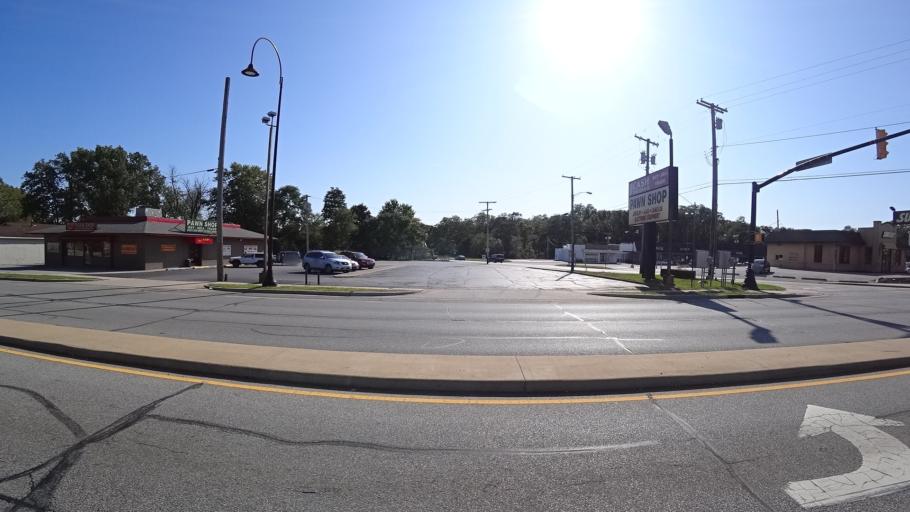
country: US
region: Indiana
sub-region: LaPorte County
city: Trail Creek
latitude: 41.7087
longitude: -86.8693
